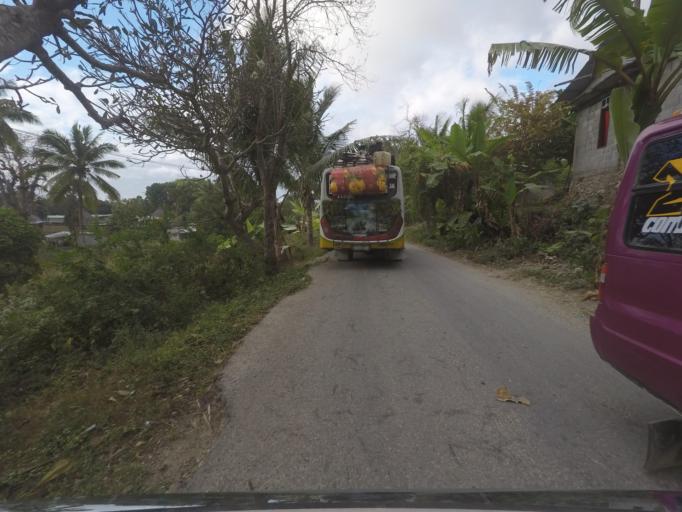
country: TL
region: Baucau
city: Baucau
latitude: -8.5221
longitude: 126.4370
